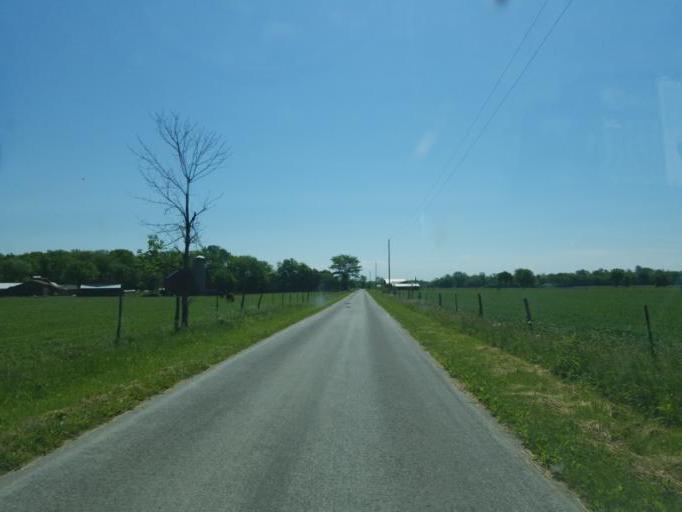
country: US
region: Ohio
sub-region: Hardin County
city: Kenton
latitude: 40.6171
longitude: -83.4873
